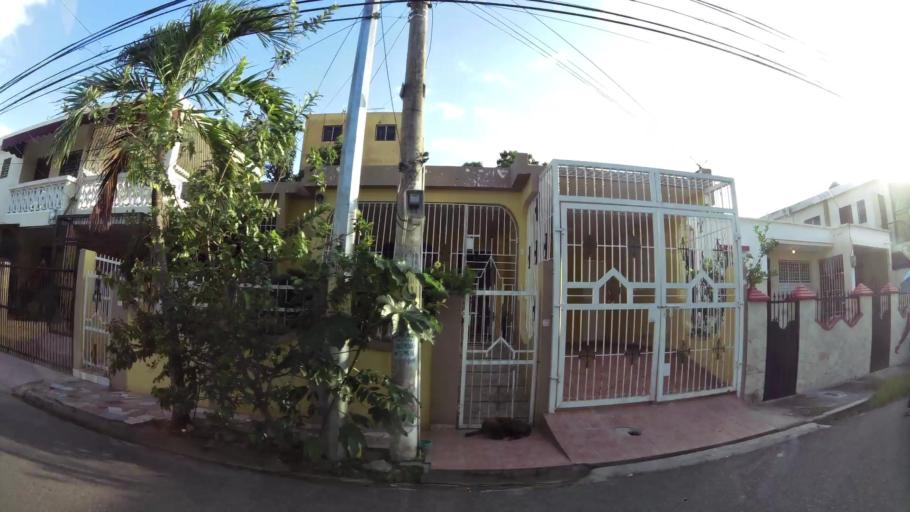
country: DO
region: Nacional
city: Ensanche Luperon
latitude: 18.5447
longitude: -69.9045
